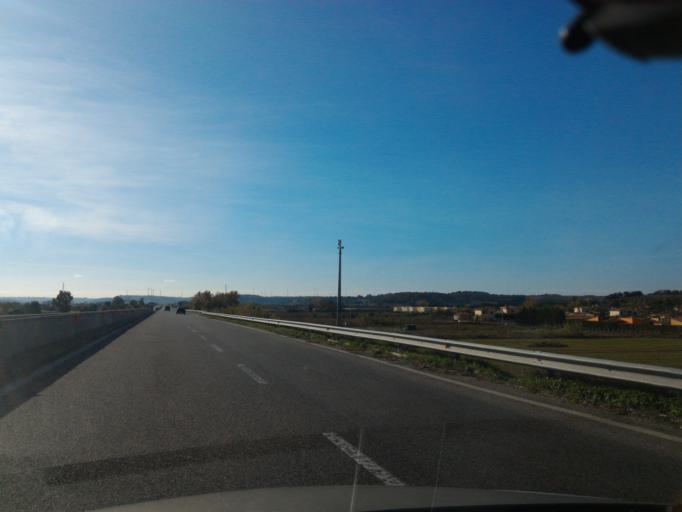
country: IT
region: Calabria
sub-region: Provincia di Crotone
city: Crotone
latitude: 39.1414
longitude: 17.0957
